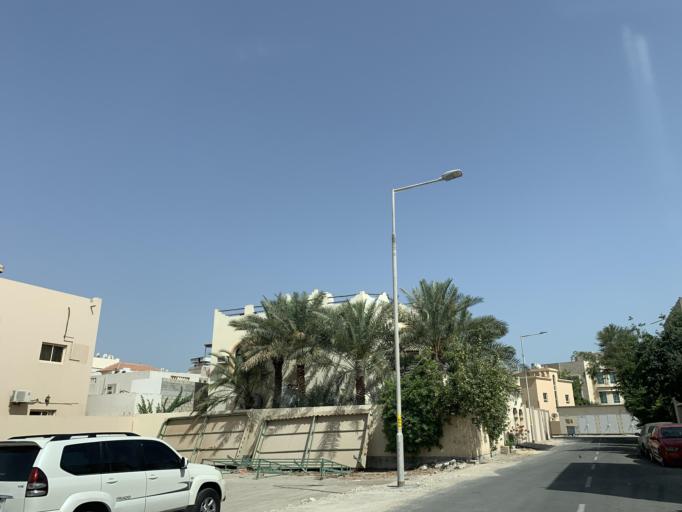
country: BH
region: Northern
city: Sitrah
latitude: 26.1446
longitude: 50.6050
